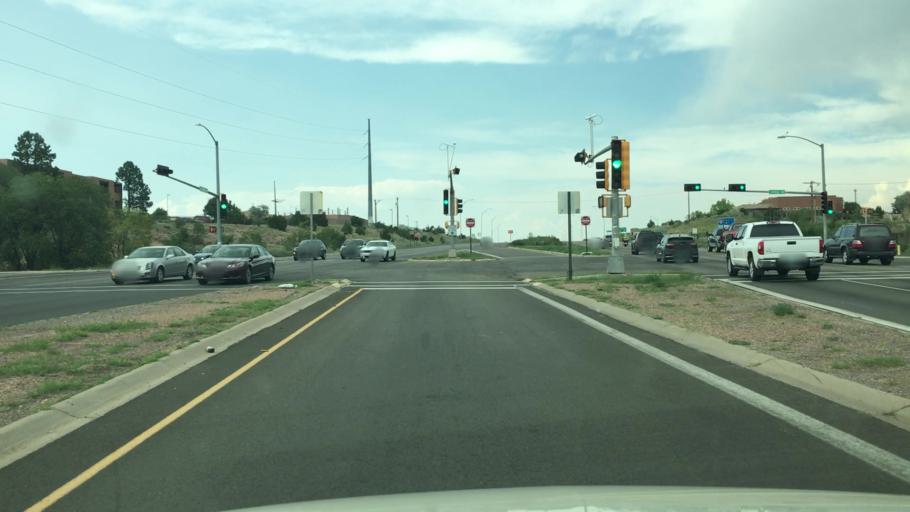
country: US
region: New Mexico
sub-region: Santa Fe County
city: Santa Fe
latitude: 35.6517
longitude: -105.9566
